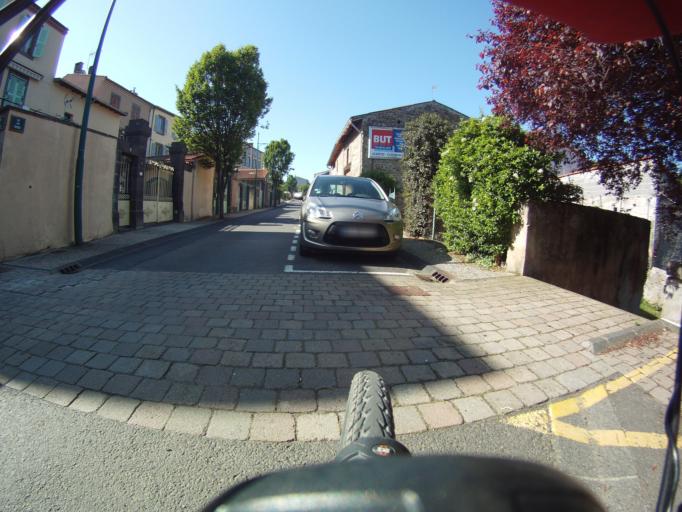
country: FR
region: Auvergne
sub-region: Departement du Puy-de-Dome
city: Dallet
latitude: 45.7691
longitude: 3.2380
